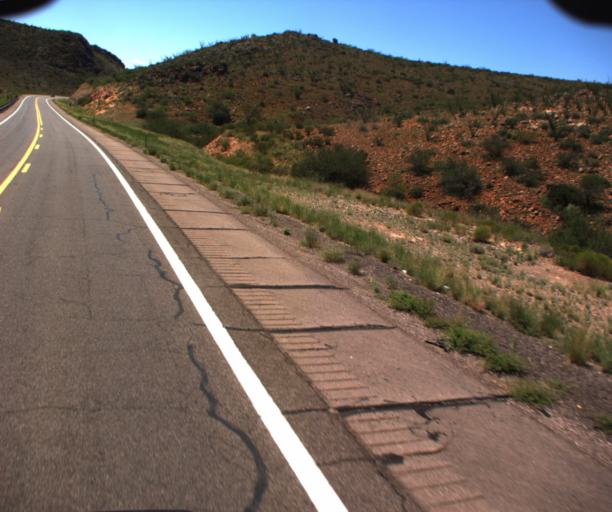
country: US
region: Arizona
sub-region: Greenlee County
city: Clifton
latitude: 32.8477
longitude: -109.3883
